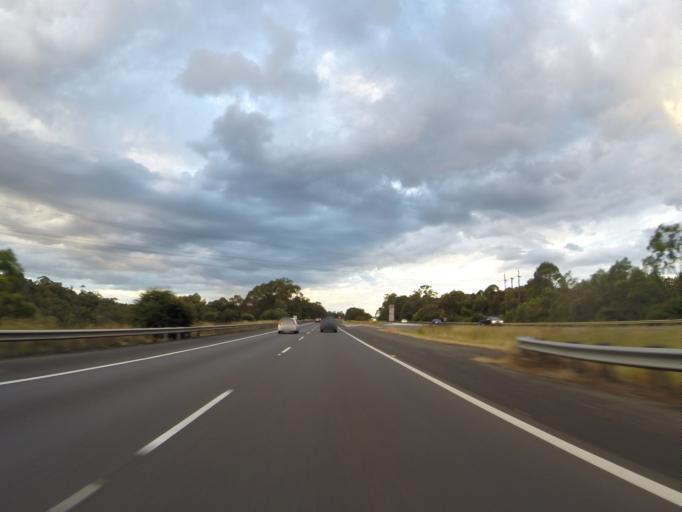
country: AU
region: New South Wales
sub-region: Wollondilly
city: Douglas Park
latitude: -34.1893
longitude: 150.7144
